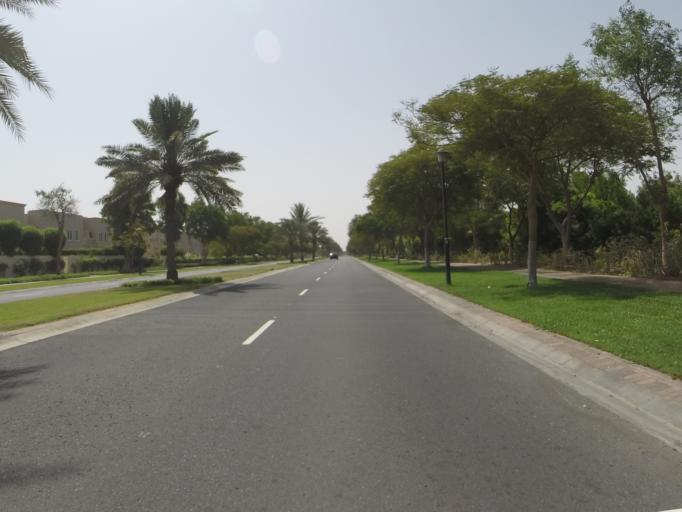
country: AE
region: Dubai
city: Dubai
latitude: 25.0619
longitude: 55.1578
